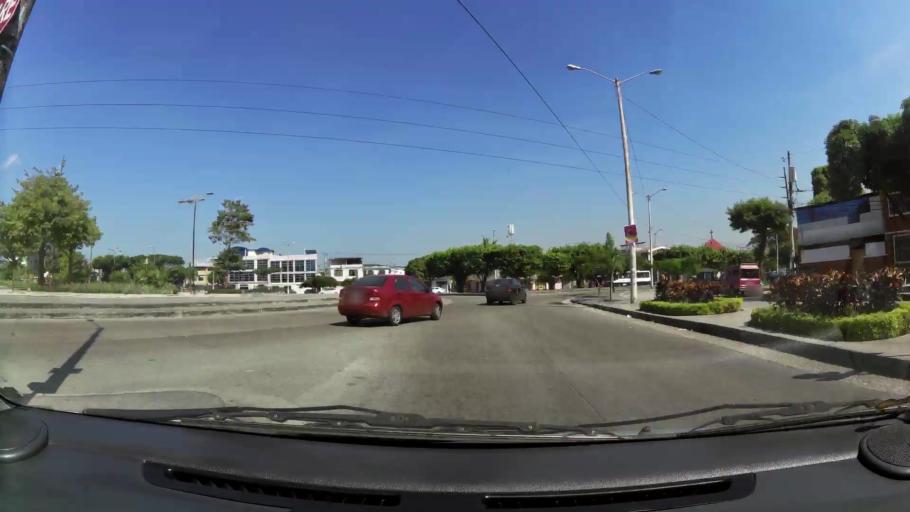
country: EC
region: Guayas
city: Eloy Alfaro
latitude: -2.1266
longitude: -79.8930
